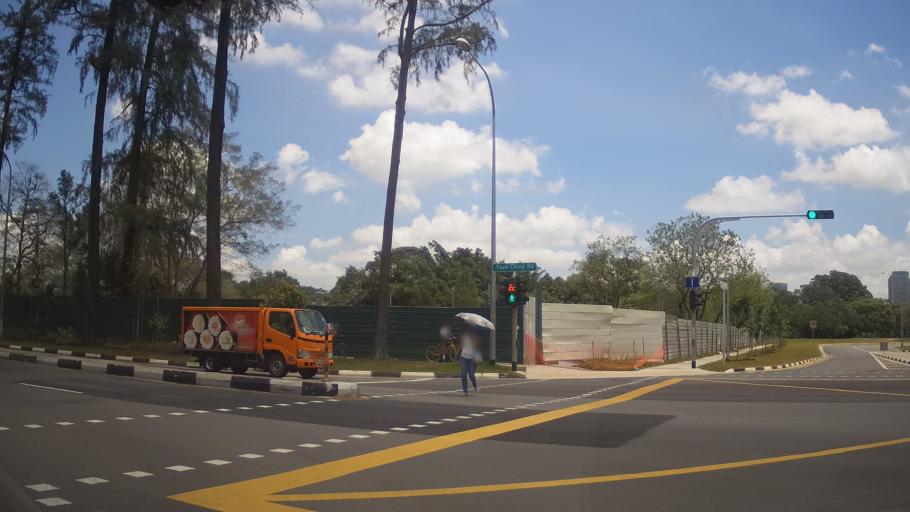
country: SG
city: Singapore
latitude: 1.3268
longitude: 103.7252
